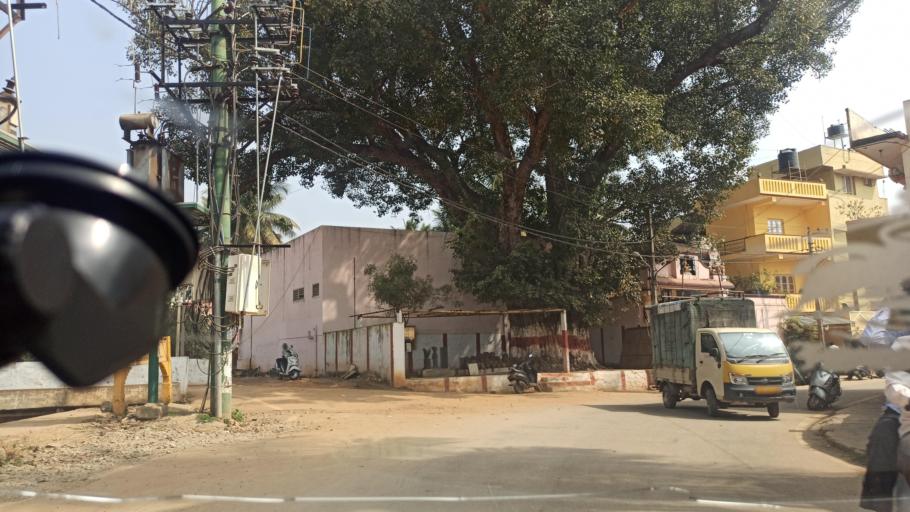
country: IN
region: Karnataka
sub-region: Bangalore Urban
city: Yelahanka
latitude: 13.1041
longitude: 77.5966
